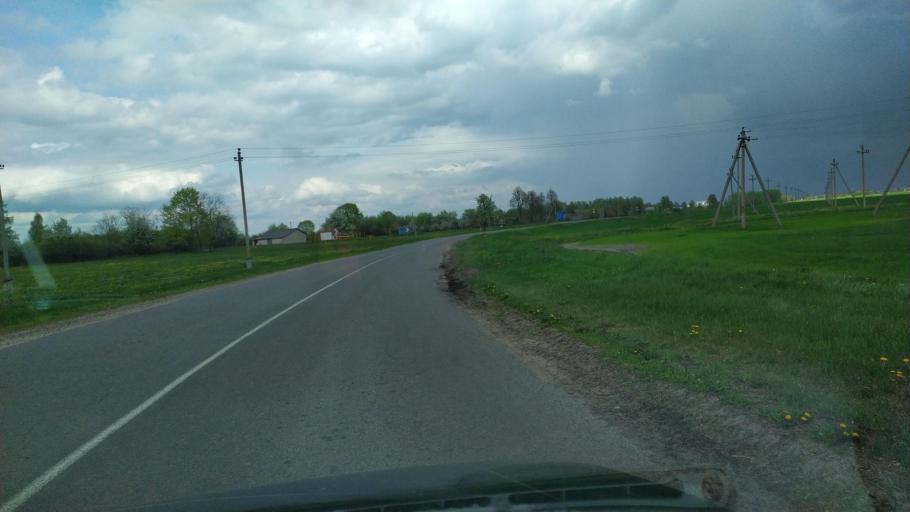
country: BY
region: Brest
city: Pruzhany
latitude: 52.6510
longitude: 24.3810
